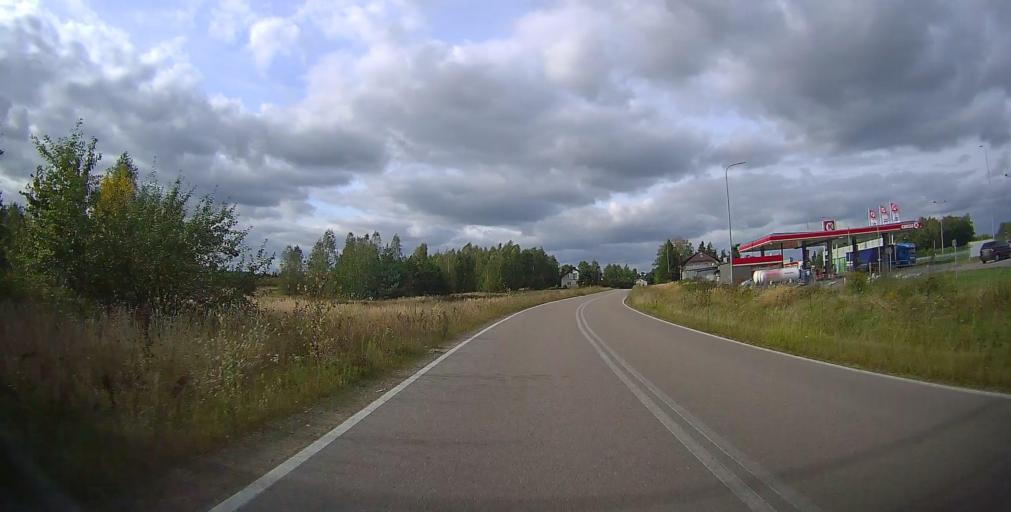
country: PL
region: Masovian Voivodeship
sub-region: Powiat grojecki
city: Goszczyn
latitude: 51.7454
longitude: 20.9091
